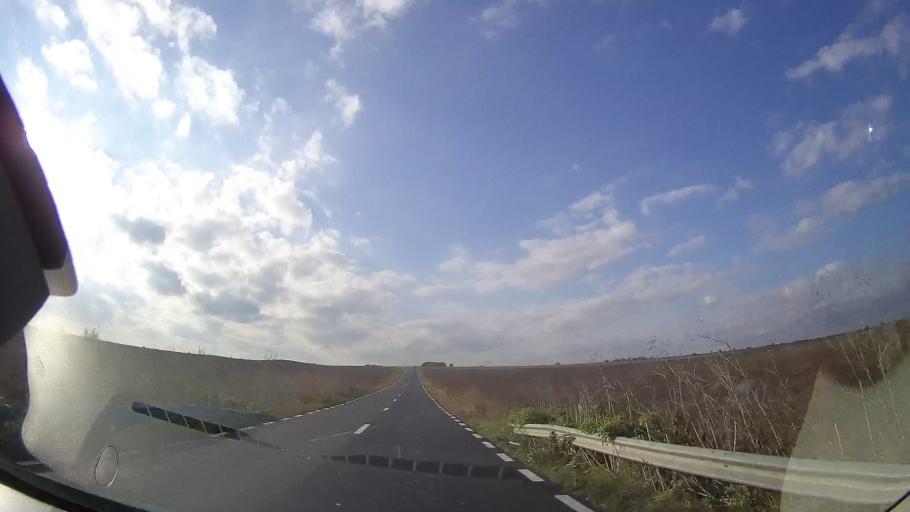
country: RO
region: Constanta
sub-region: Comuna Limanu
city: Limanu
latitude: 43.8247
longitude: 28.5013
